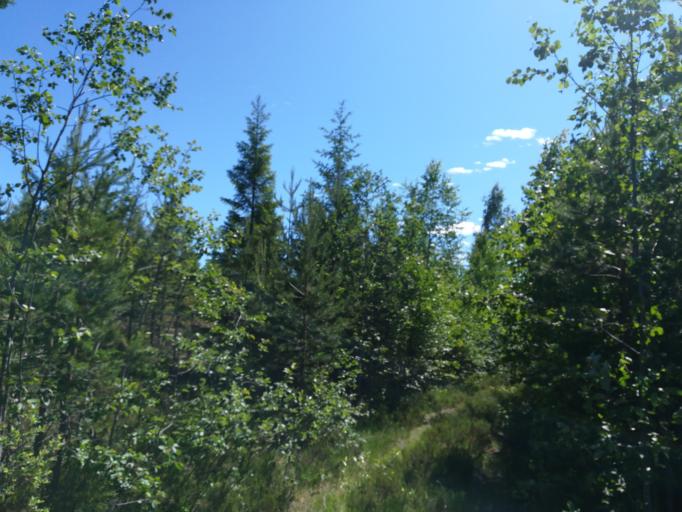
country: FI
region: Southern Savonia
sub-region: Mikkeli
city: Puumala
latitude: 61.6200
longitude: 28.1615
